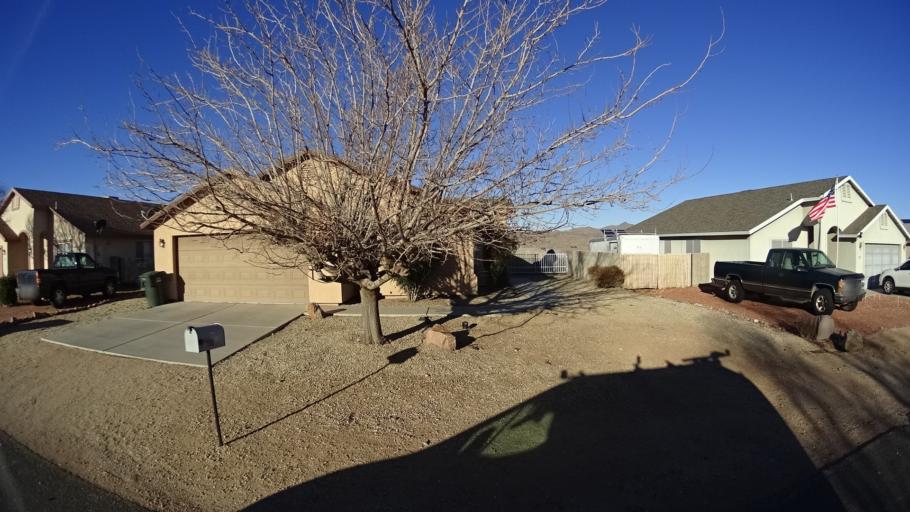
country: US
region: Arizona
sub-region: Mohave County
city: Kingman
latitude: 35.2114
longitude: -114.0045
